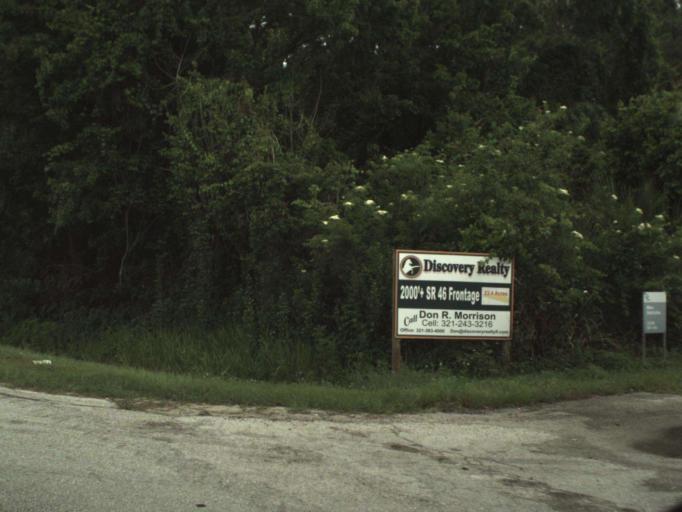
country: US
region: Florida
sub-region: Brevard County
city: Mims
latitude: 28.6644
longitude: -80.8529
